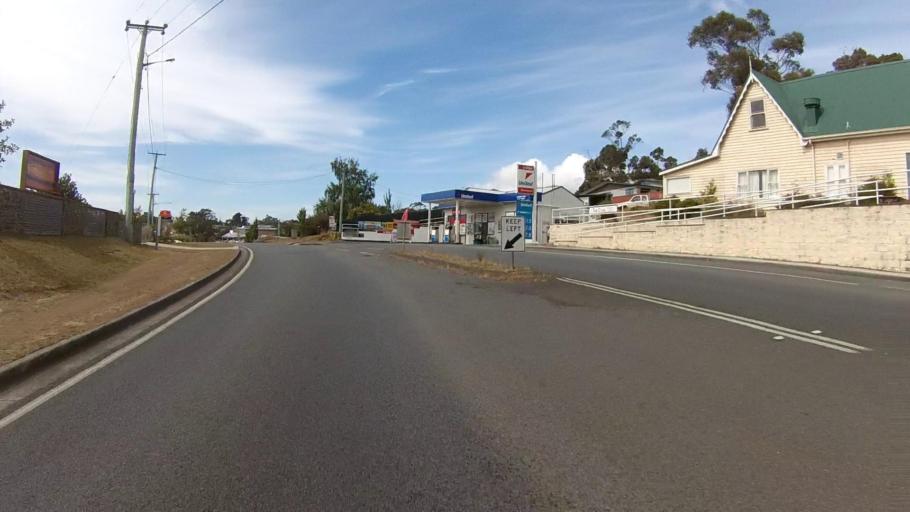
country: AU
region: Tasmania
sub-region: Kingborough
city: Kettering
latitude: -43.1230
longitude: 147.2454
